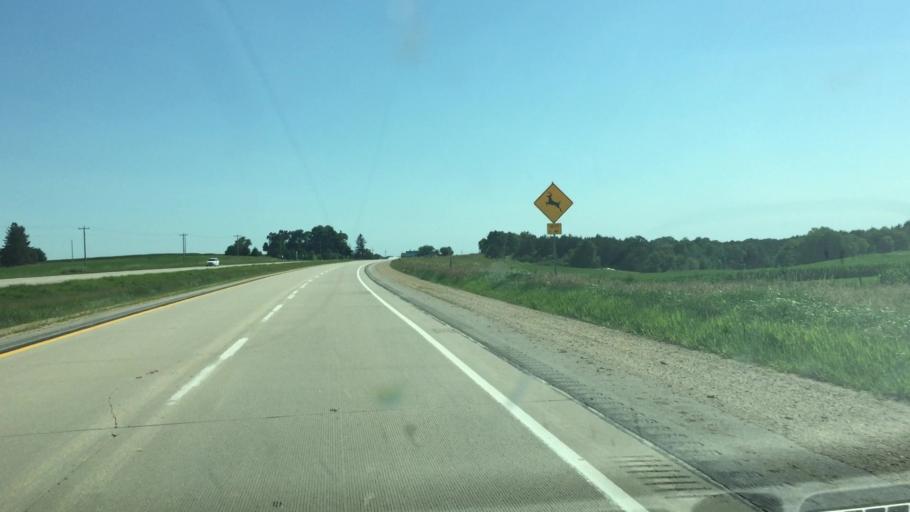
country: US
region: Iowa
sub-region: Jones County
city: Monticello
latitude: 42.2707
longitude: -91.1419
